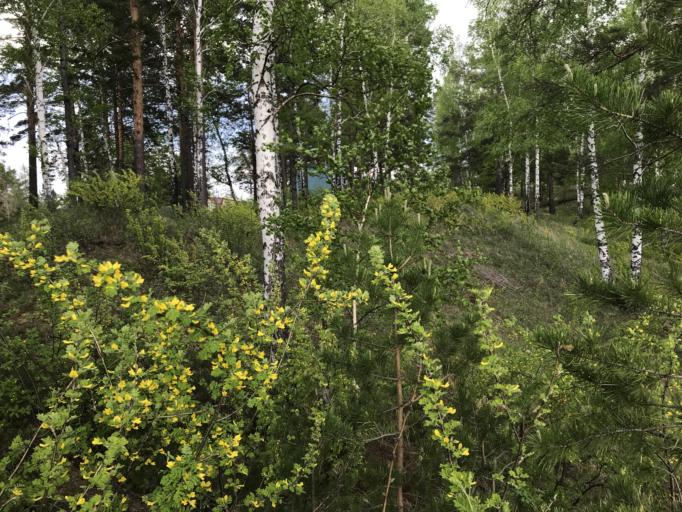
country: RU
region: Krasnoyarskiy
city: Ovsyanka
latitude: 56.0270
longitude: 92.5631
